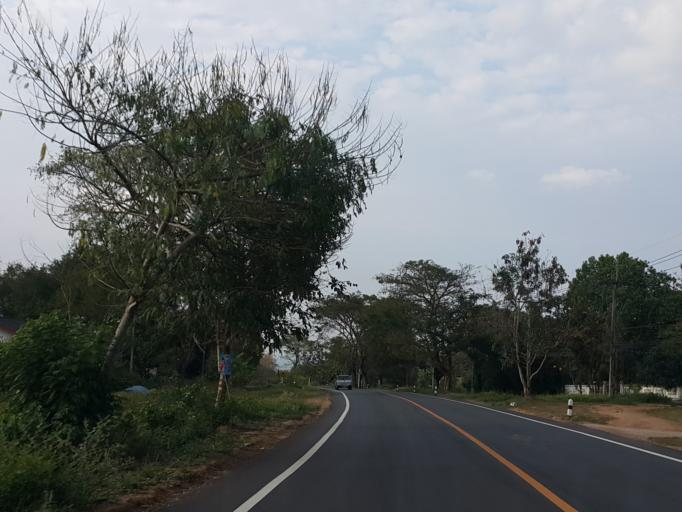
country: TH
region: Lampang
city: Lampang
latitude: 18.4863
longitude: 99.4726
